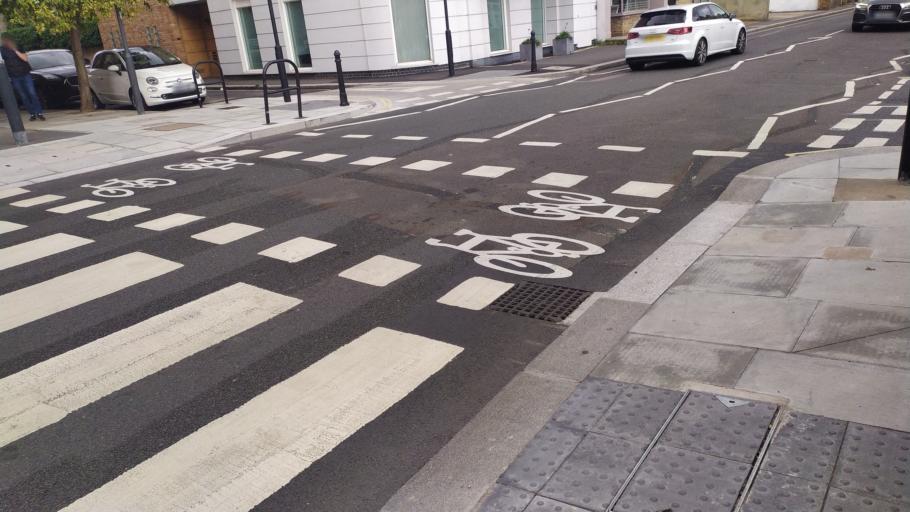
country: GB
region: England
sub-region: Greater London
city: Wandsworth
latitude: 51.4708
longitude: -0.2075
